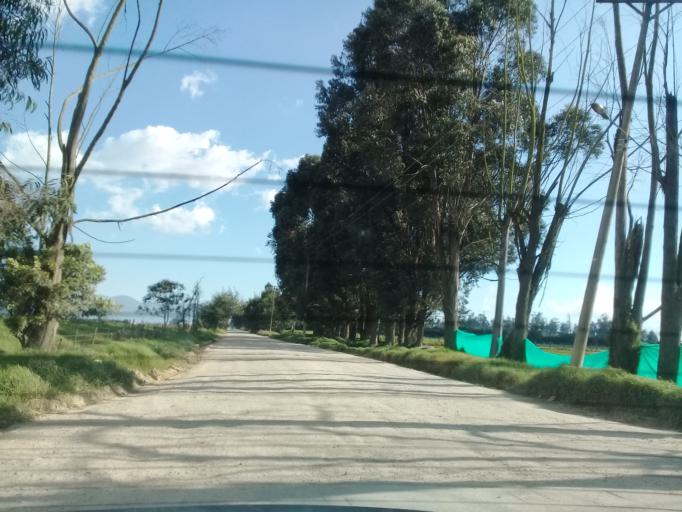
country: CO
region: Cundinamarca
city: Funza
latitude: 4.7215
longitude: -74.1799
